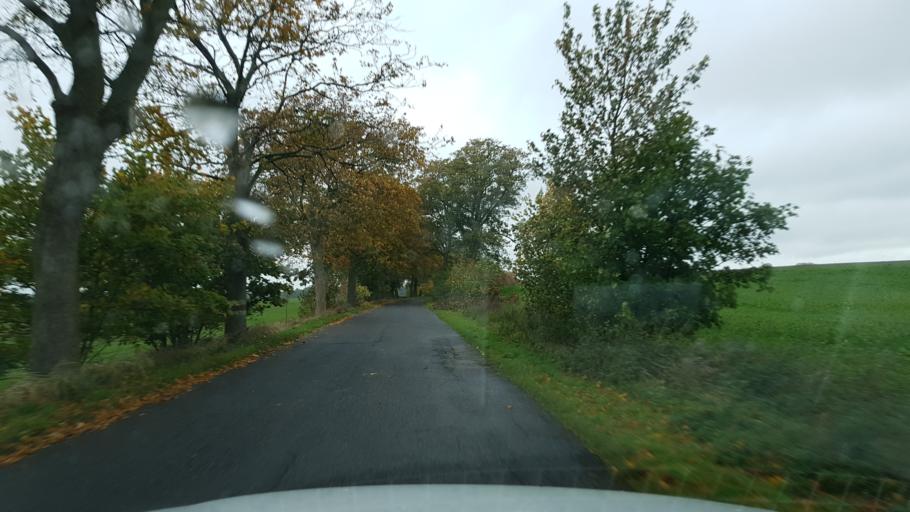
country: PL
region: West Pomeranian Voivodeship
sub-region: Powiat mysliborski
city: Mysliborz
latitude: 52.9772
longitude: 14.8775
